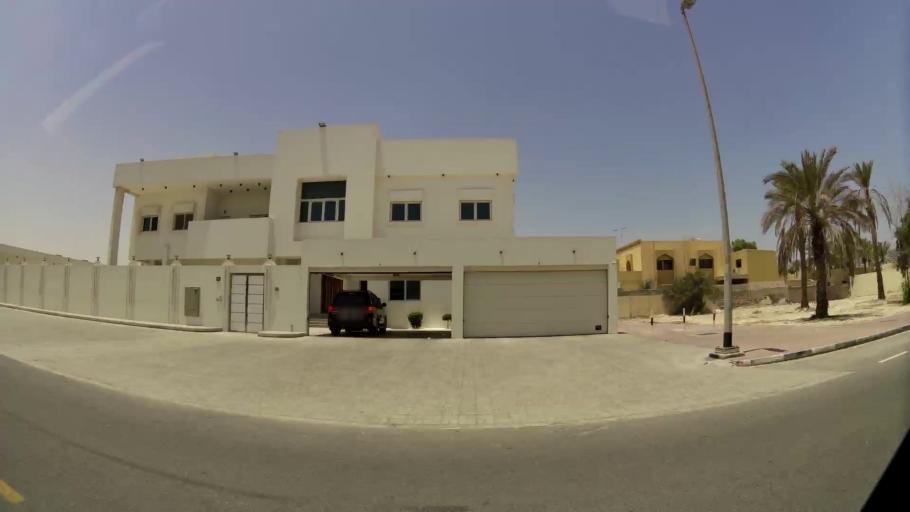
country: AE
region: Dubai
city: Dubai
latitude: 25.1911
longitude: 55.2479
